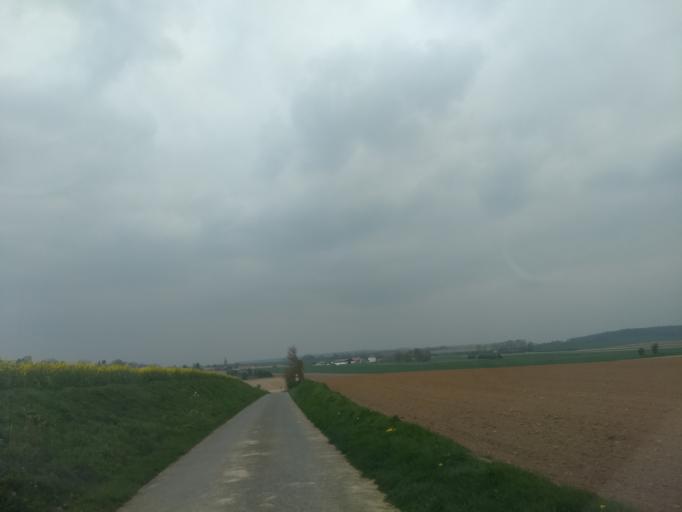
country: FR
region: Nord-Pas-de-Calais
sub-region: Departement du Pas-de-Calais
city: Mont-Saint-Eloi
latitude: 50.3446
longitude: 2.7016
